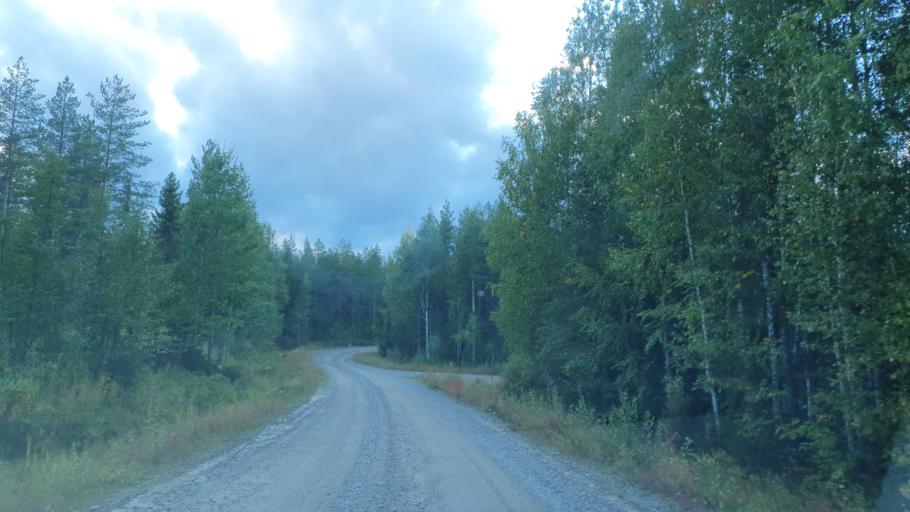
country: FI
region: Kainuu
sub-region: Kehys-Kainuu
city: Kuhmo
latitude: 64.3364
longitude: 29.9205
